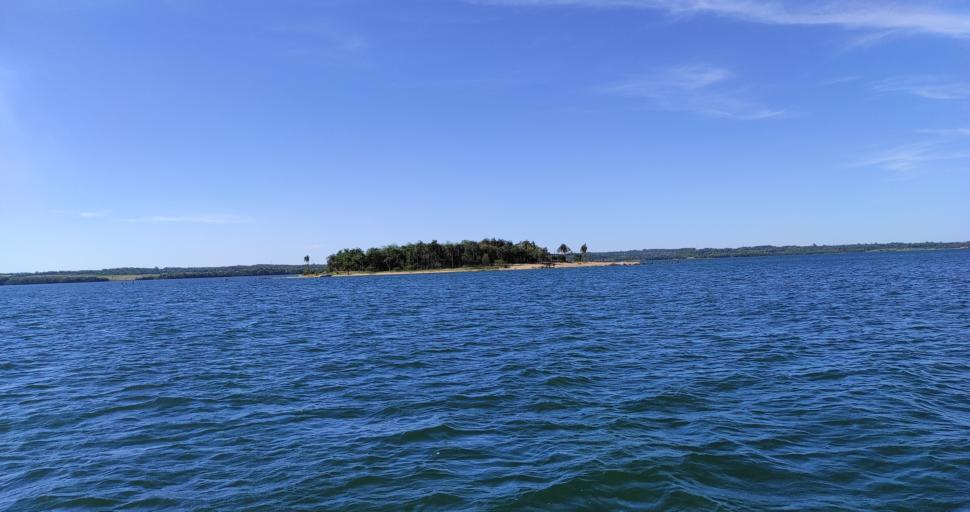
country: PY
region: Itapua
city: San Juan del Parana
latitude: -27.3432
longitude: -55.9498
